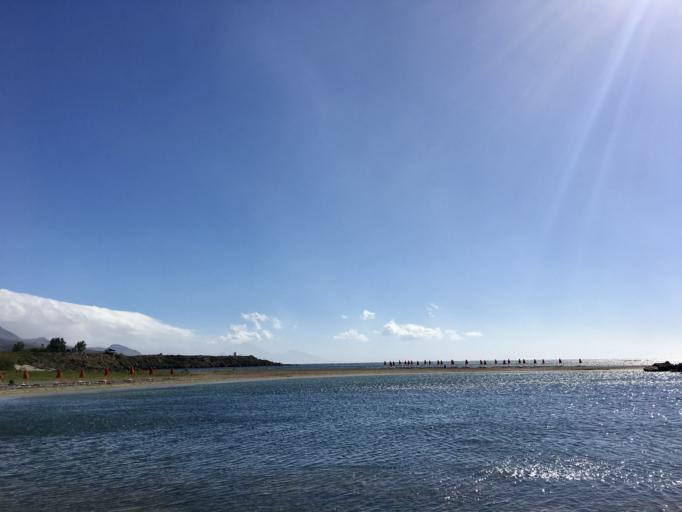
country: GR
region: Crete
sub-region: Nomos Chanias
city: Chora Sfakion
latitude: 35.1806
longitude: 24.2314
